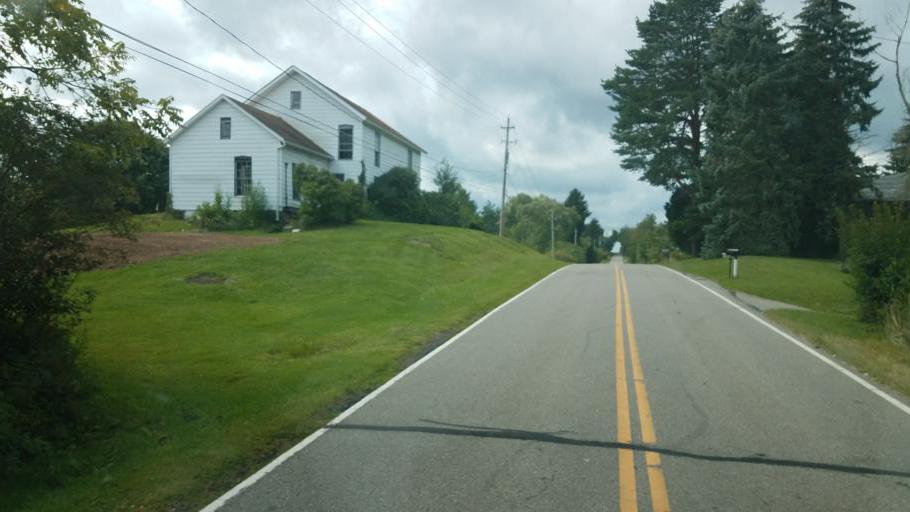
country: US
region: Ohio
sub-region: Geauga County
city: Burton
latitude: 41.5203
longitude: -81.1274
